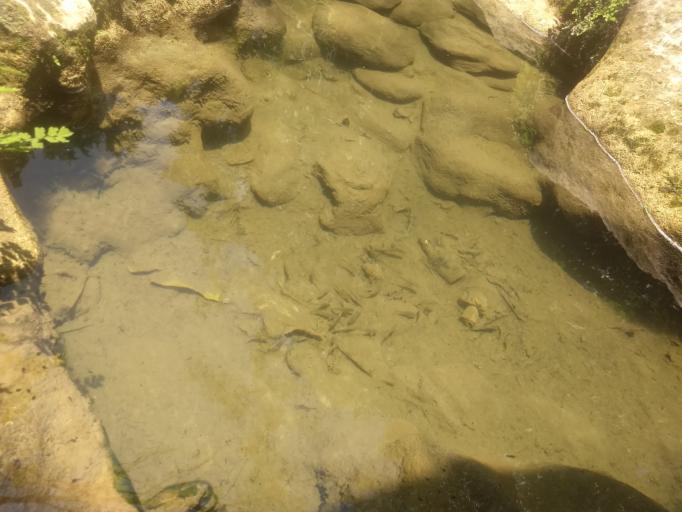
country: MX
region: Nuevo Leon
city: Santiago
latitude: 25.3688
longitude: -100.1582
